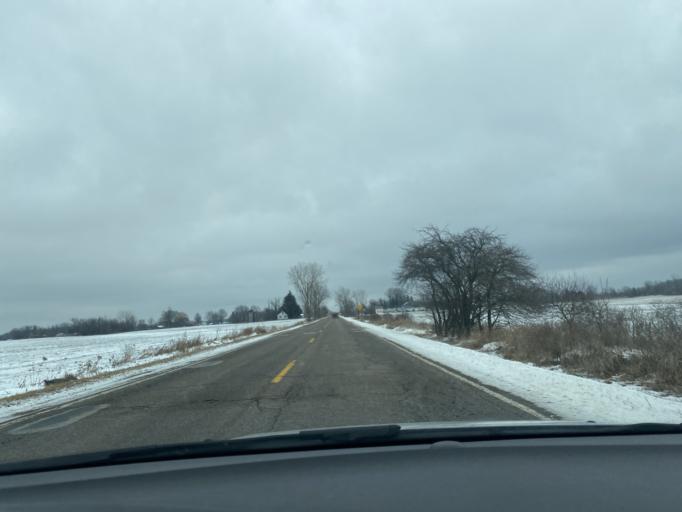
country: US
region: Michigan
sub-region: Sanilac County
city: Brown City
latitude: 43.2104
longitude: -83.0863
